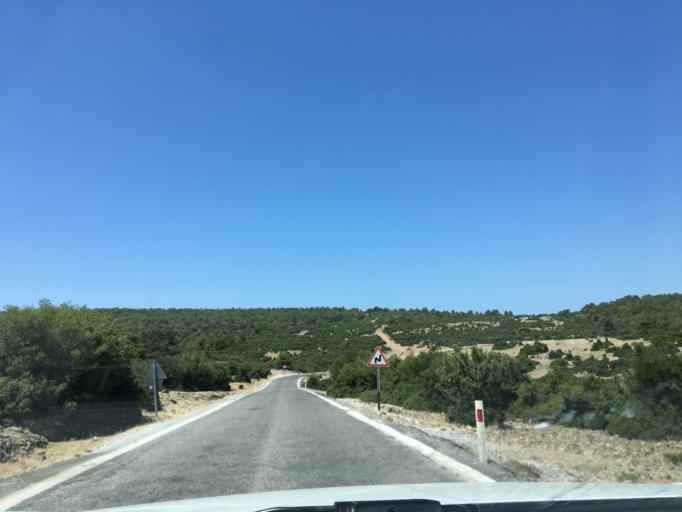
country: TR
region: Canakkale
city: Gulpinar
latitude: 39.4958
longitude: 26.1466
